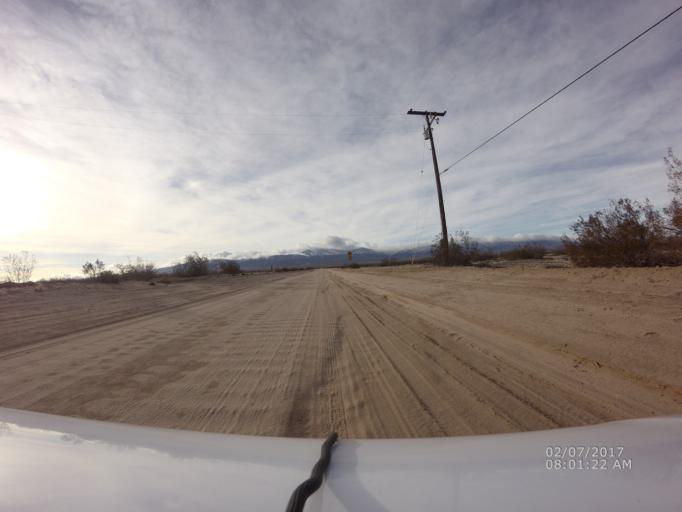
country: US
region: California
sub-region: Los Angeles County
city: Lake Los Angeles
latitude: 34.5747
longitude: -117.7736
